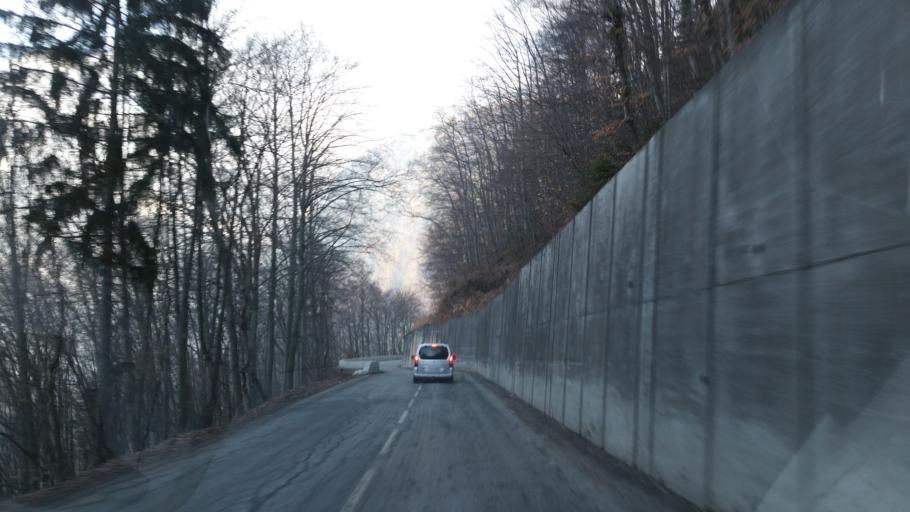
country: FR
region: Rhone-Alpes
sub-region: Departement de la Savoie
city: Saint-Jean-de-Maurienne
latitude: 45.2673
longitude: 6.3253
